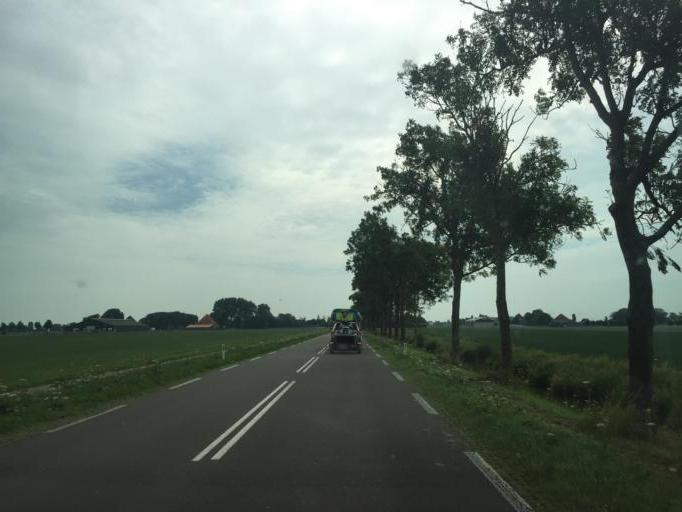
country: NL
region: North Holland
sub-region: Gemeente Beemster
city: Halfweg
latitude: 52.5895
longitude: 4.9290
